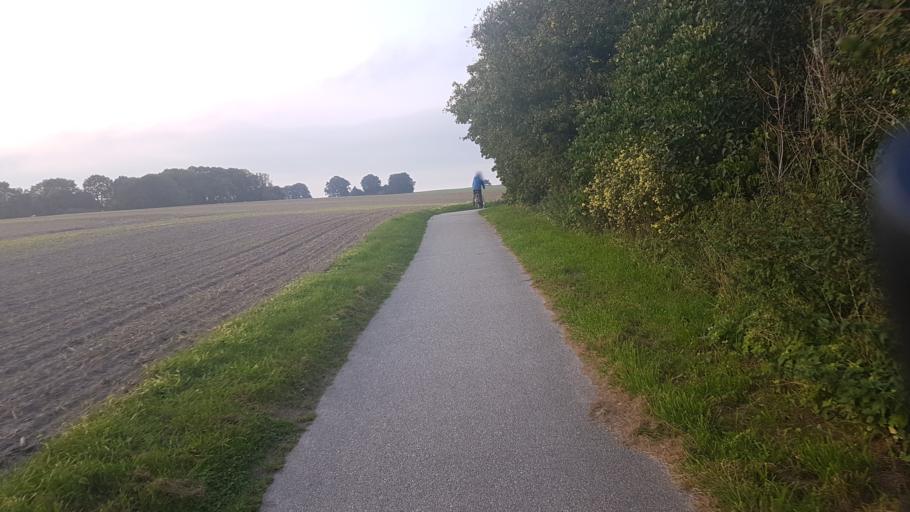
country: DE
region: Mecklenburg-Vorpommern
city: Ostseebad Binz
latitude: 54.3436
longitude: 13.5579
